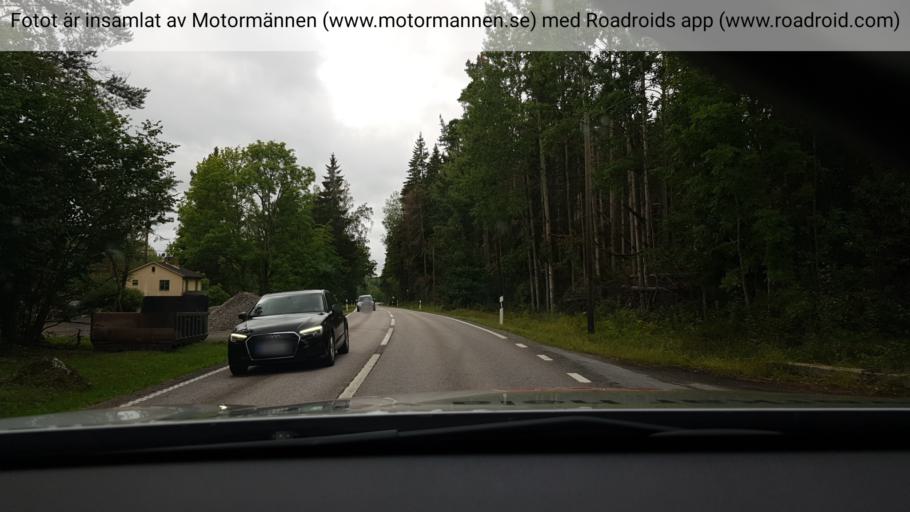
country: SE
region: Stockholm
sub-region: Norrtalje Kommun
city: Rimbo
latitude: 59.7349
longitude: 18.4436
